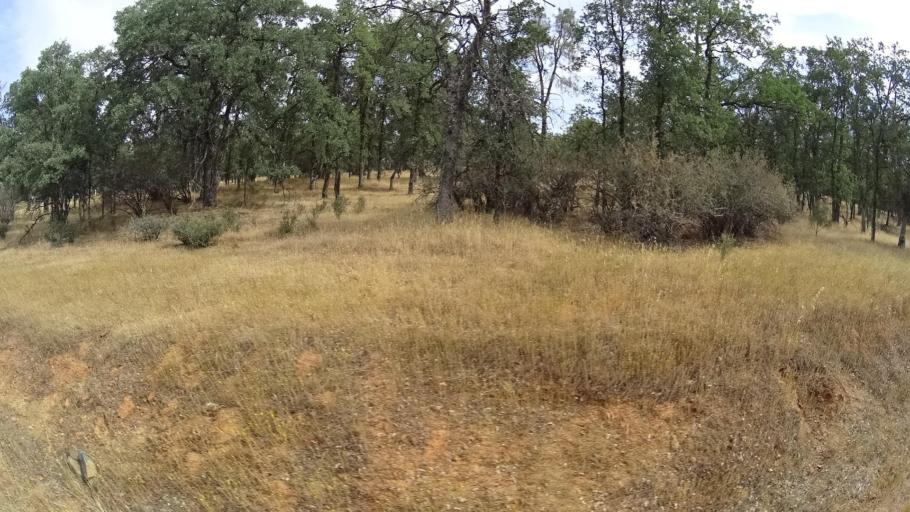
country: US
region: California
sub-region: Mariposa County
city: Midpines
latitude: 37.5340
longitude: -119.9672
